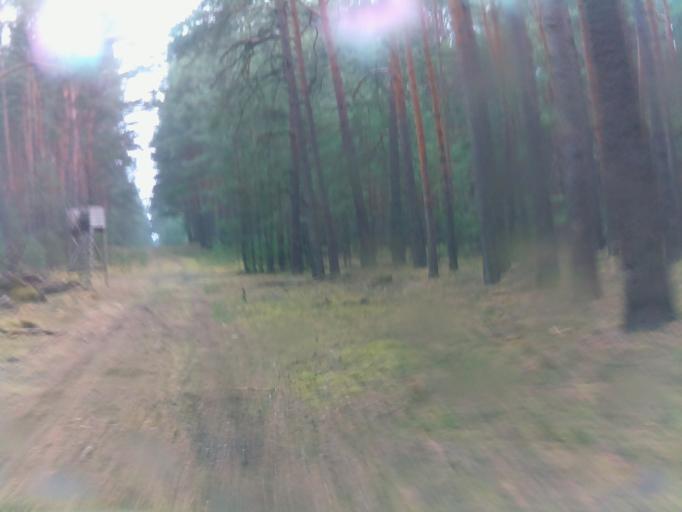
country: DE
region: Brandenburg
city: Jamlitz
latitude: 51.9805
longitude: 14.3878
